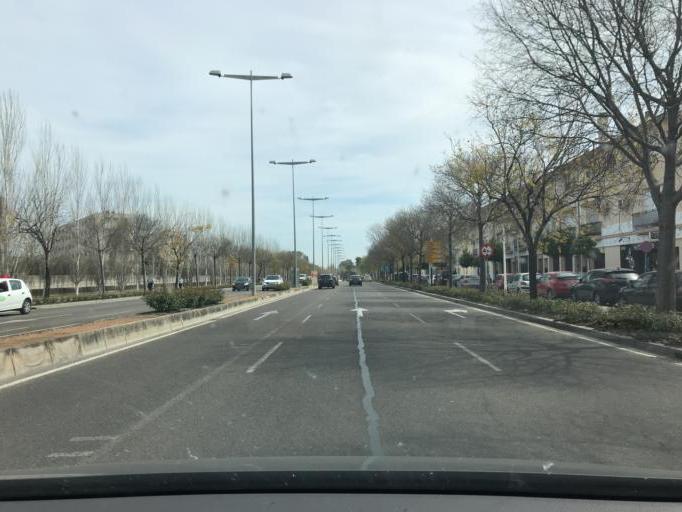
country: ES
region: Andalusia
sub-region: Province of Cordoba
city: Cordoba
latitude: 37.8962
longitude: -4.7720
